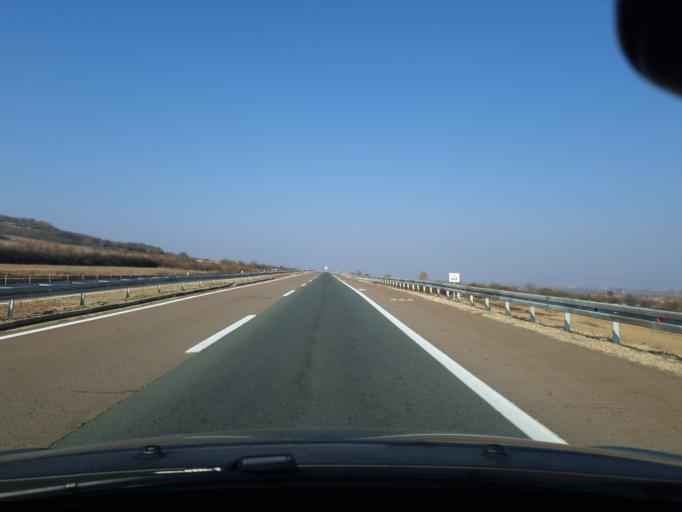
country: RS
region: Central Serbia
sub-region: Nisavski Okrug
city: Doljevac
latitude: 43.2513
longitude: 21.8159
